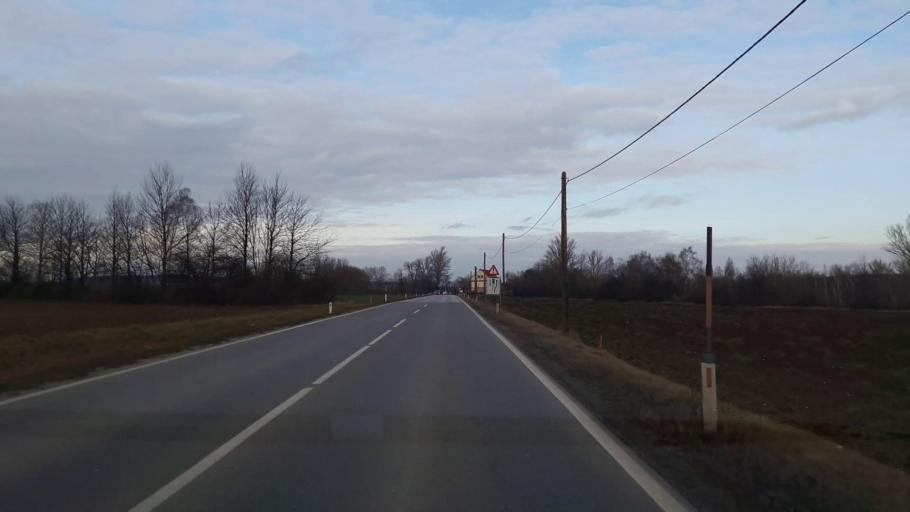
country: AT
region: Lower Austria
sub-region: Politischer Bezirk Mistelbach
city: Staatz
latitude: 48.6372
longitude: 16.5159
